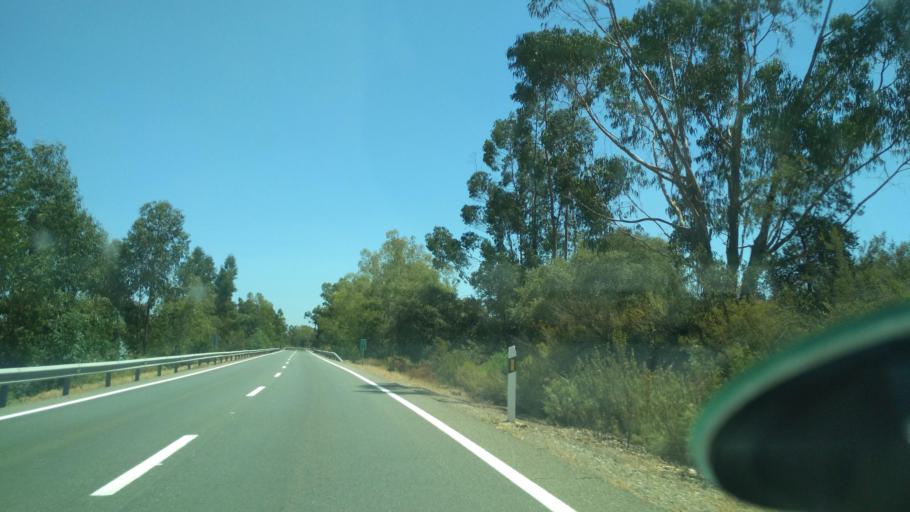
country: ES
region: Andalusia
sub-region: Provincia de Huelva
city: Campofrio
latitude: 37.8299
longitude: -6.5650
